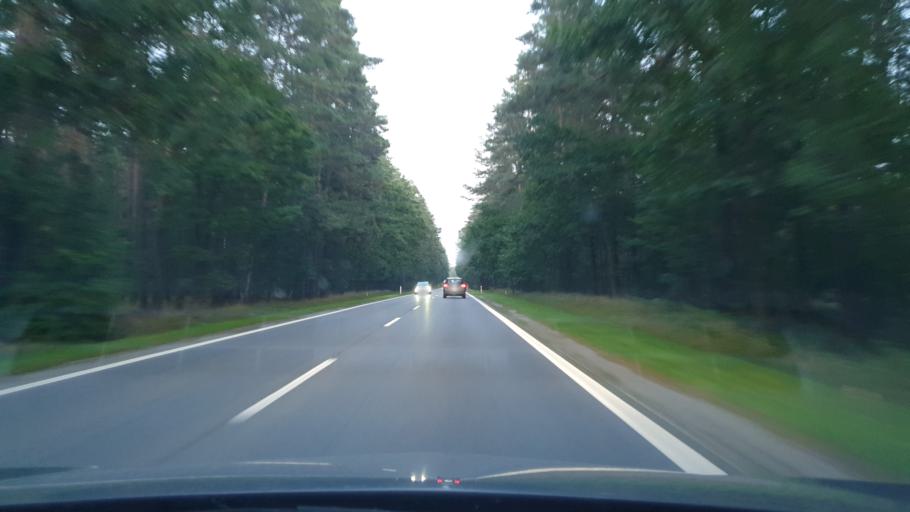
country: PL
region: Pomeranian Voivodeship
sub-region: Powiat wejherowski
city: Luzino
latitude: 54.5688
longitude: 18.0075
